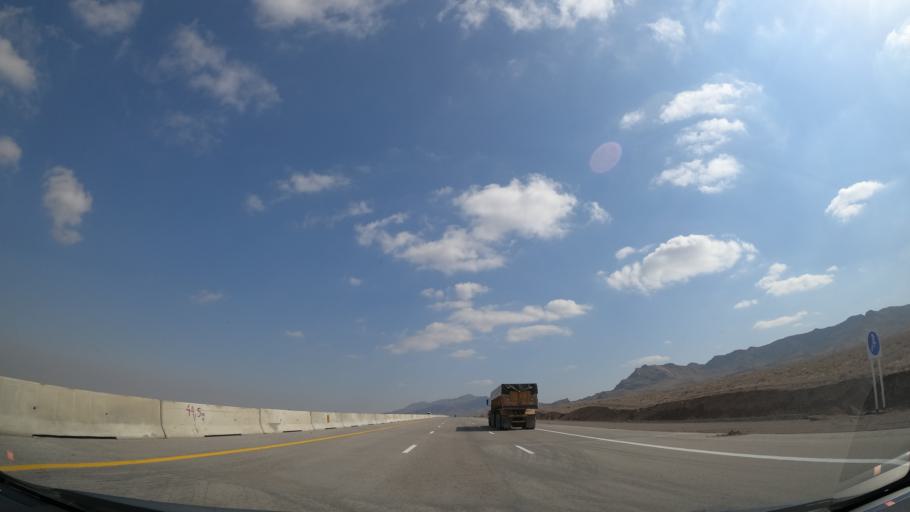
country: IR
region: Alborz
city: Eshtehard
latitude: 35.7094
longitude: 50.5995
